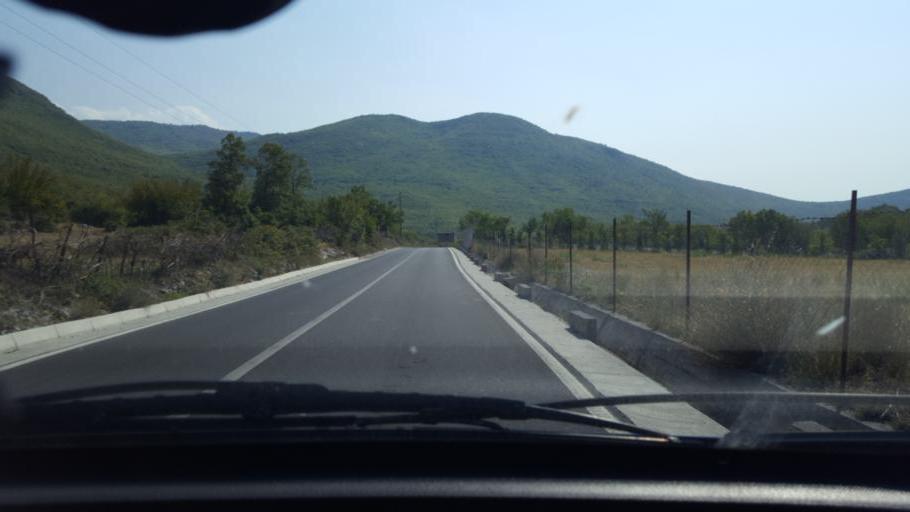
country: AL
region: Shkoder
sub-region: Rrethi i Malesia e Madhe
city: Kastrat
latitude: 42.3893
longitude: 19.4925
